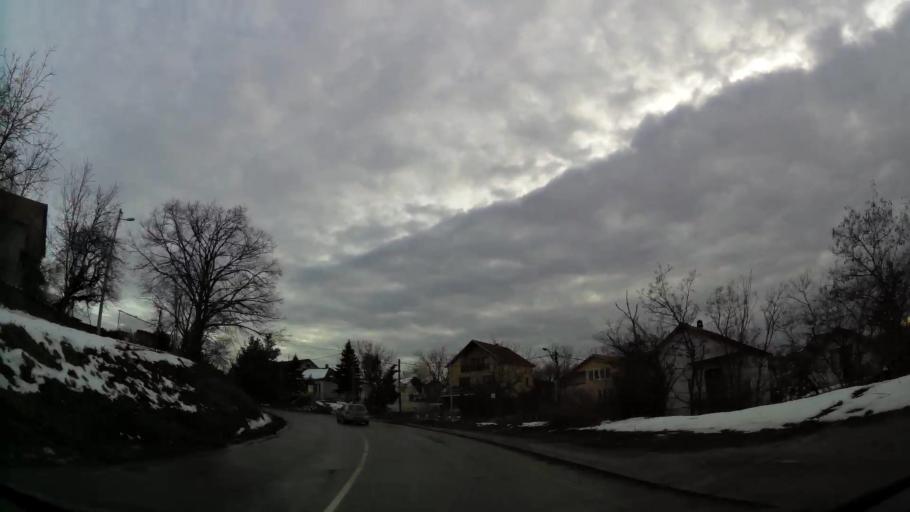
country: RS
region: Central Serbia
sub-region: Belgrade
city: Rakovica
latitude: 44.7231
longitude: 20.4957
